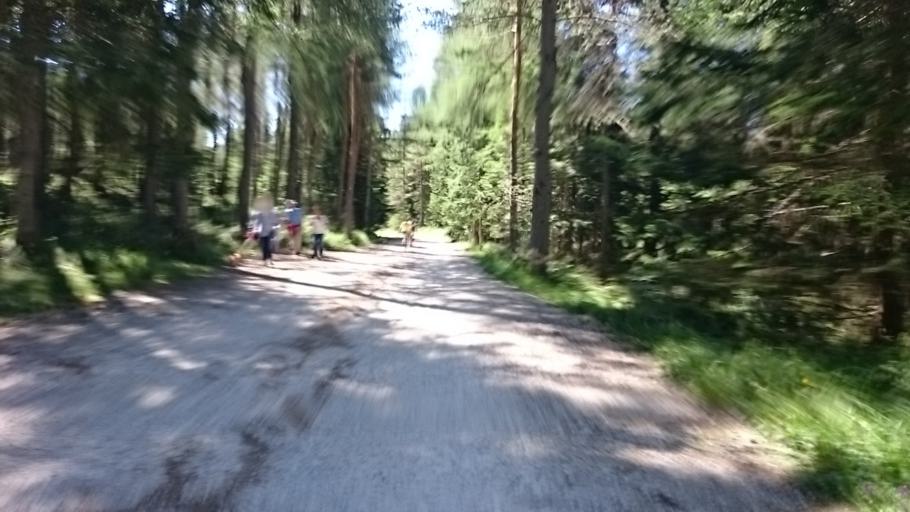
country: IT
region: Veneto
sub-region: Provincia di Belluno
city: Cortina d'Ampezzo
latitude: 46.5605
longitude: 12.1265
